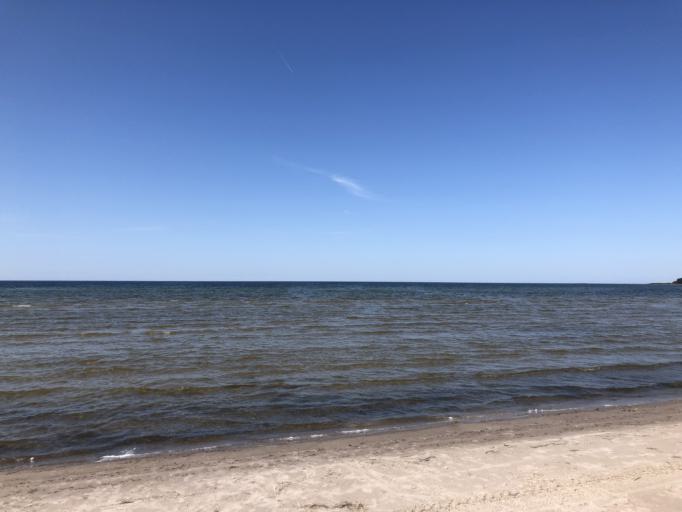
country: EE
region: Hiiumaa
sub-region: Kaerdla linn
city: Kardla
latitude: 58.7754
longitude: 22.4776
